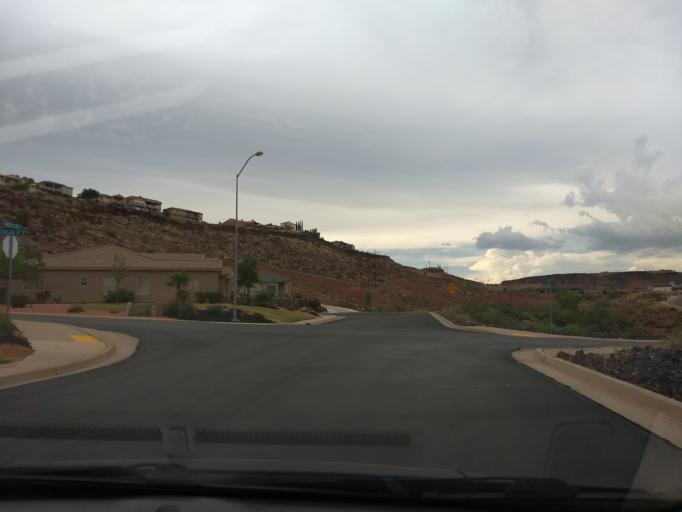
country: US
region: Utah
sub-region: Washington County
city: Saint George
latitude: 37.1109
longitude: -113.5475
